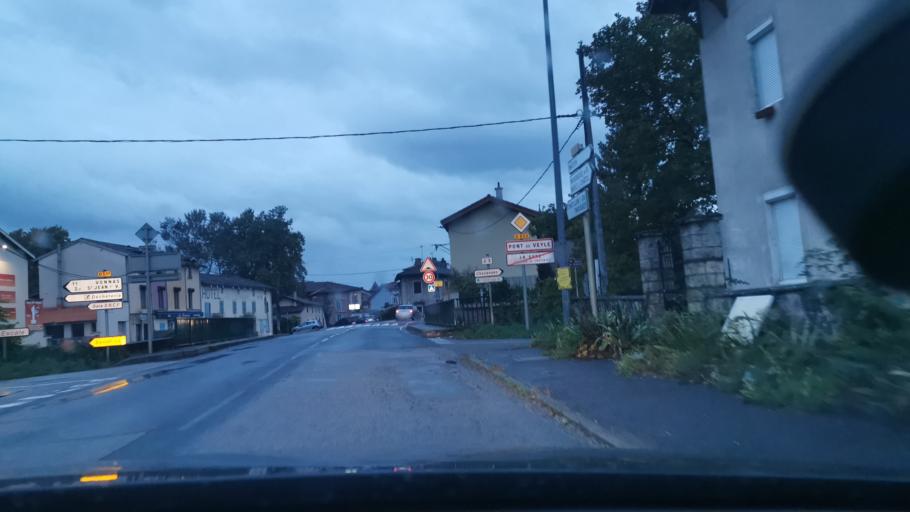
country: FR
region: Rhone-Alpes
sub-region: Departement de l'Ain
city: Pont-de-Veyle
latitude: 46.2671
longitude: 4.8910
